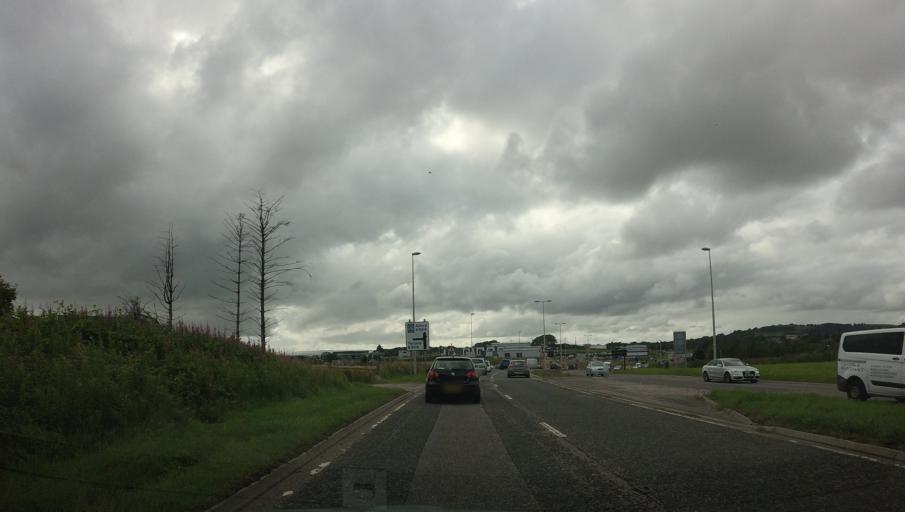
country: GB
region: Scotland
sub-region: Aberdeenshire
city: Westhill
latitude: 57.1471
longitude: -2.2617
